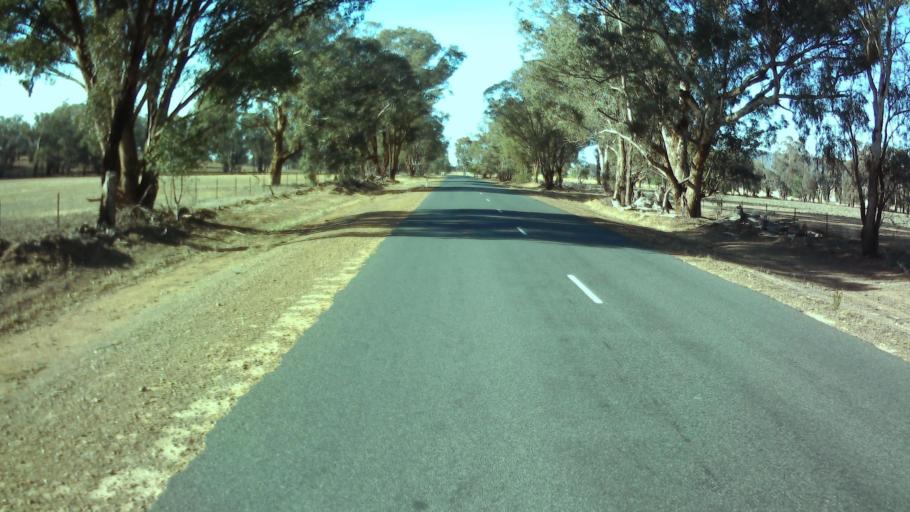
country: AU
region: New South Wales
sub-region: Weddin
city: Grenfell
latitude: -33.9398
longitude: 148.1368
